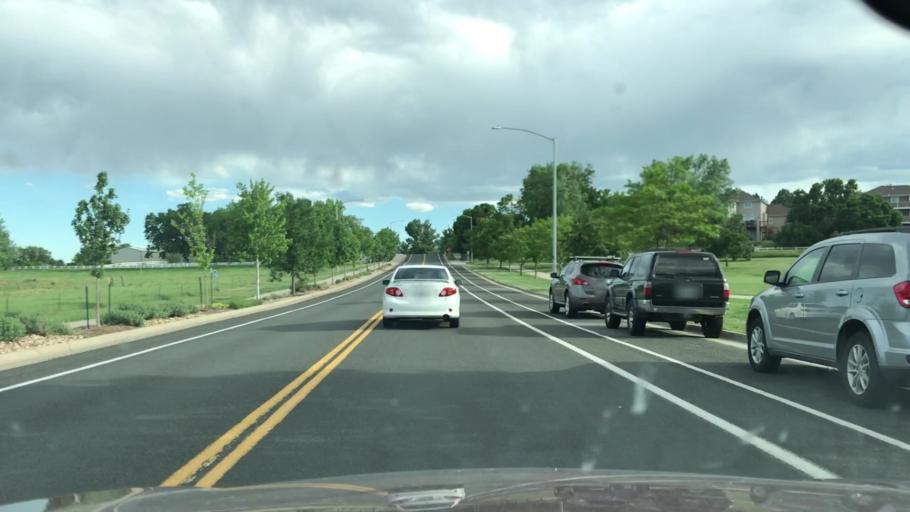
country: US
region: Colorado
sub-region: Broomfield County
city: Broomfield
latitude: 39.9464
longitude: -105.0624
